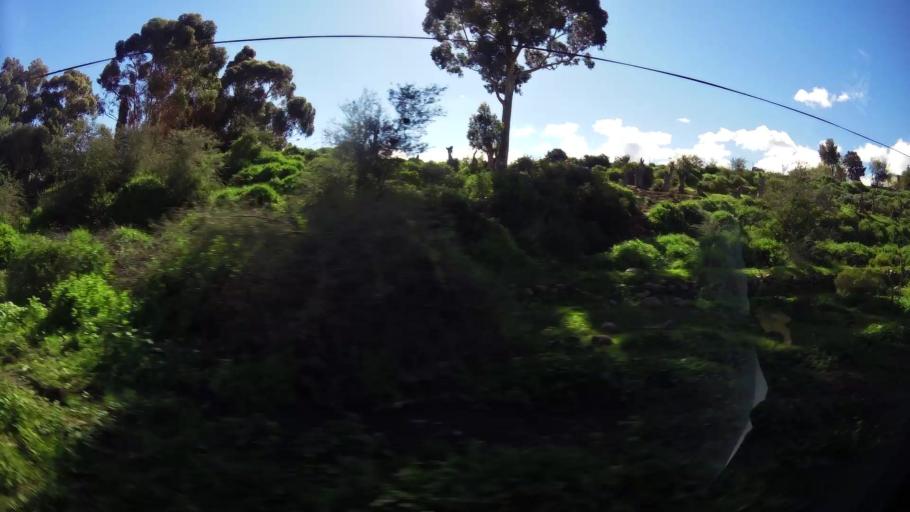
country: ZA
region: Western Cape
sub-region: Cape Winelands District Municipality
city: Ashton
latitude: -33.7943
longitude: 19.8976
